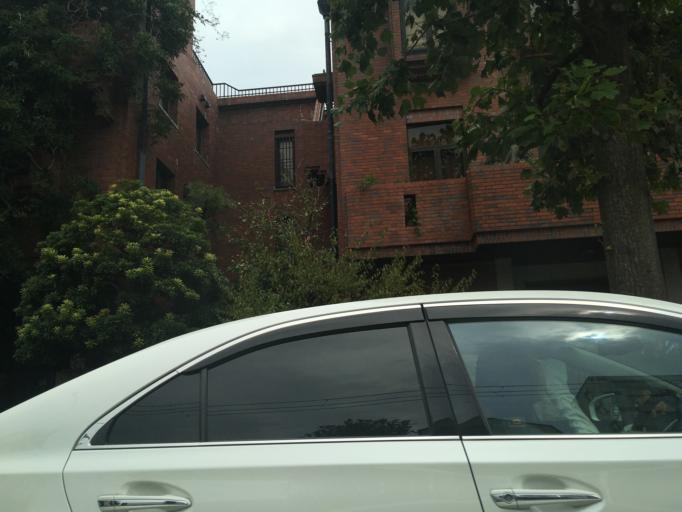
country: JP
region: Hyogo
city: Ashiya
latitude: 34.7213
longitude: 135.2516
